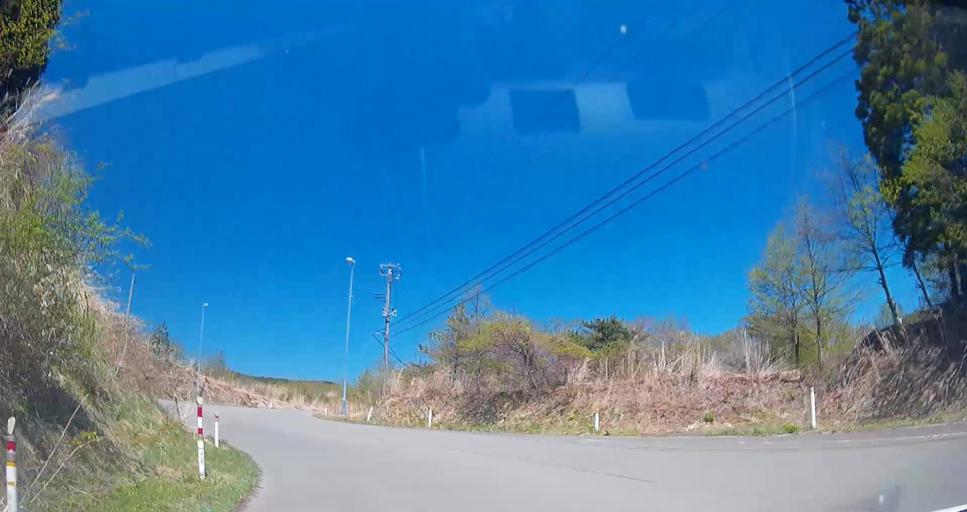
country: JP
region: Aomori
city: Mutsu
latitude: 41.2555
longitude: 141.3882
